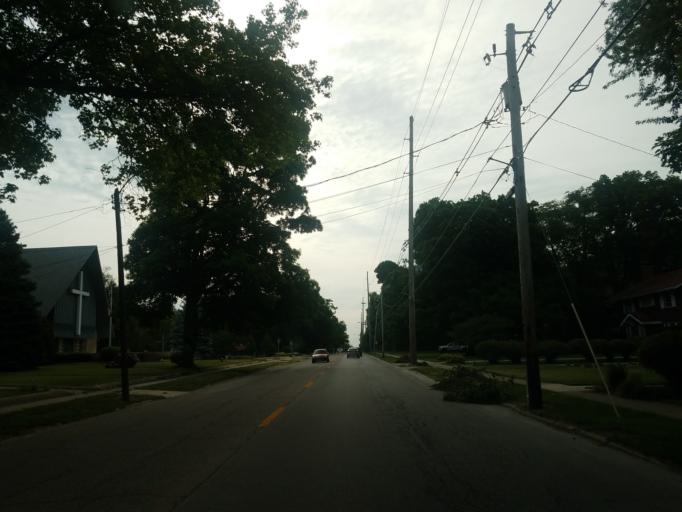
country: US
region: Illinois
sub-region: McLean County
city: Bloomington
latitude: 40.4739
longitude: -88.9674
